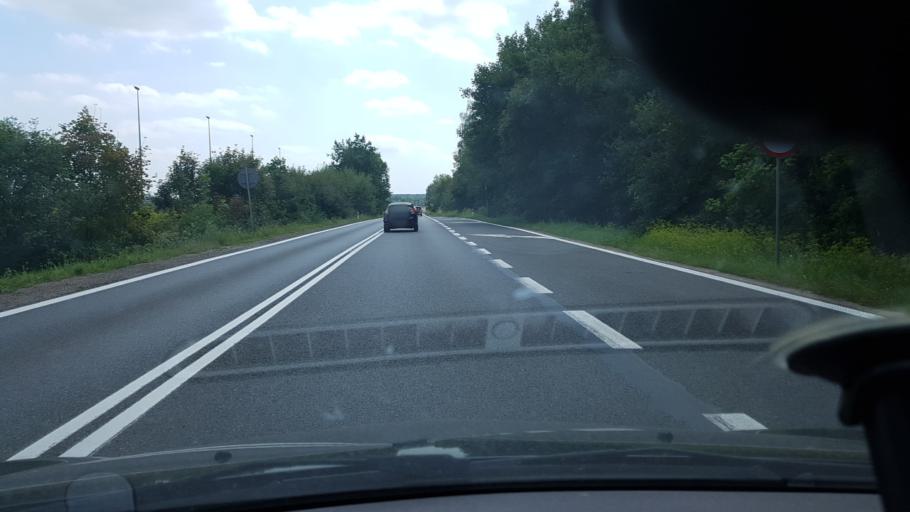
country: PL
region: Silesian Voivodeship
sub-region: Powiat bierunsko-ledzinski
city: Bierun
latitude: 50.0982
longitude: 19.0994
